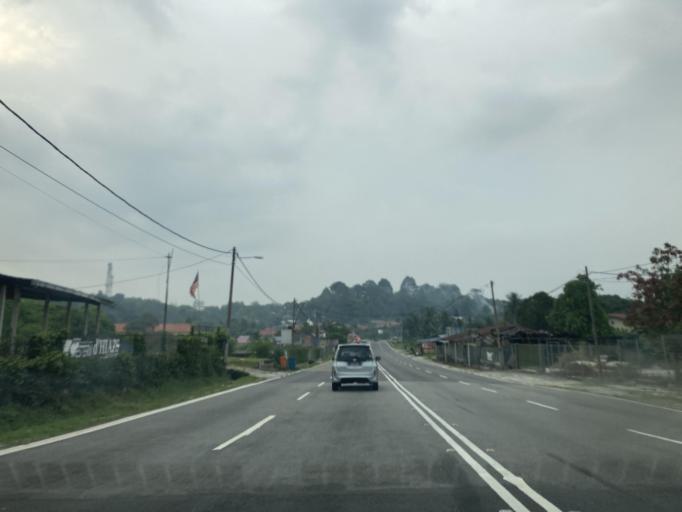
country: MY
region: Selangor
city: Kuang
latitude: 3.2094
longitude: 101.5371
